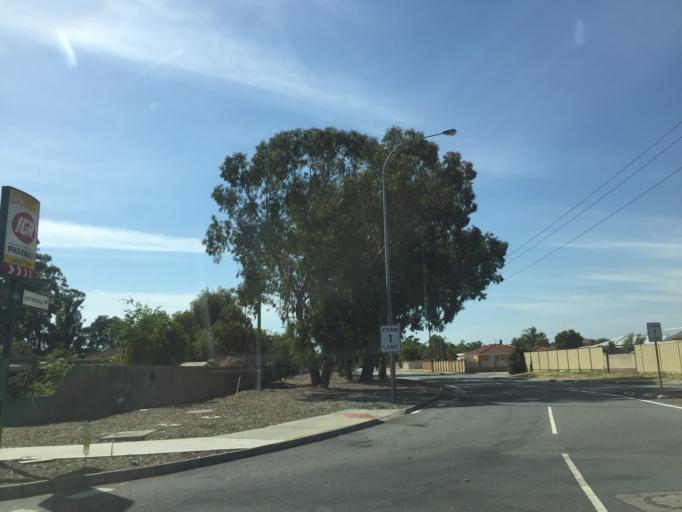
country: AU
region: Western Australia
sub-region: Gosnells
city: Thornlie
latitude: -32.0751
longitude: 115.9614
